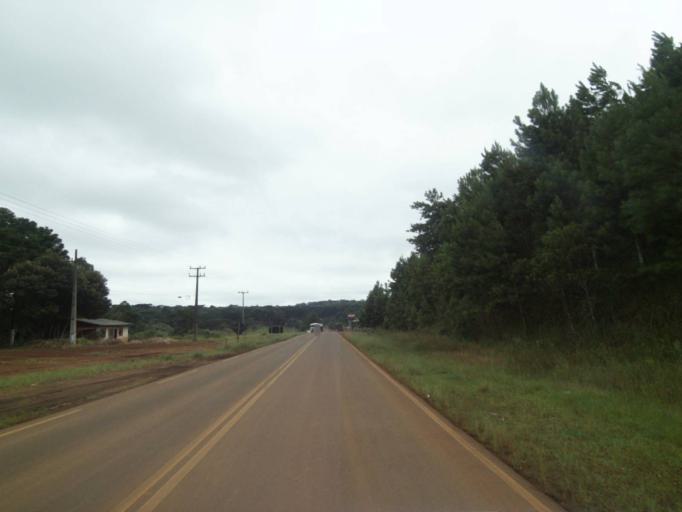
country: BR
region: Parana
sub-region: Pitanga
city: Pitanga
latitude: -24.9324
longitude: -51.8777
